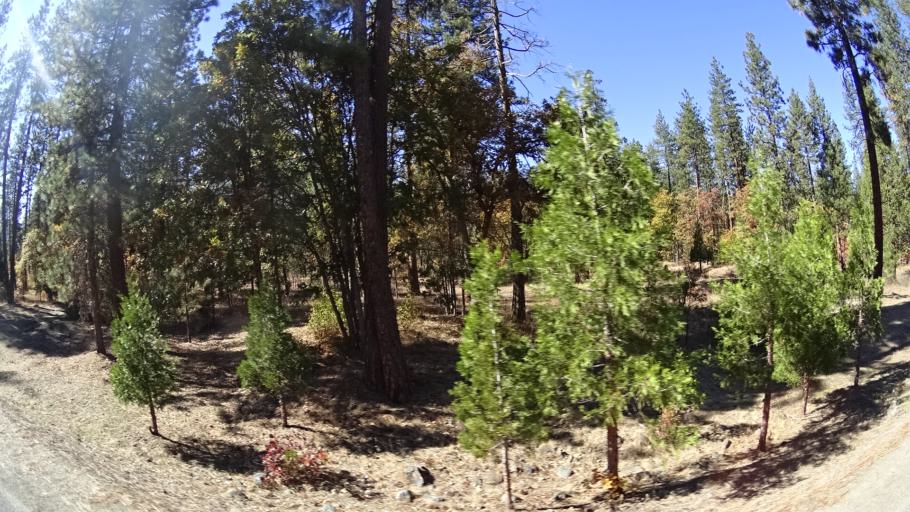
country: US
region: California
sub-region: Siskiyou County
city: Yreka
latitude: 41.5960
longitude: -122.9741
